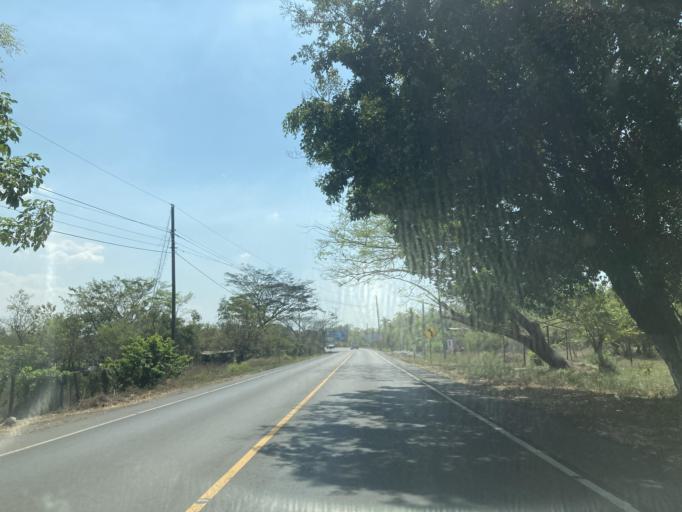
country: GT
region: Escuintla
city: Guanagazapa
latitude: 14.2025
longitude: -90.7132
